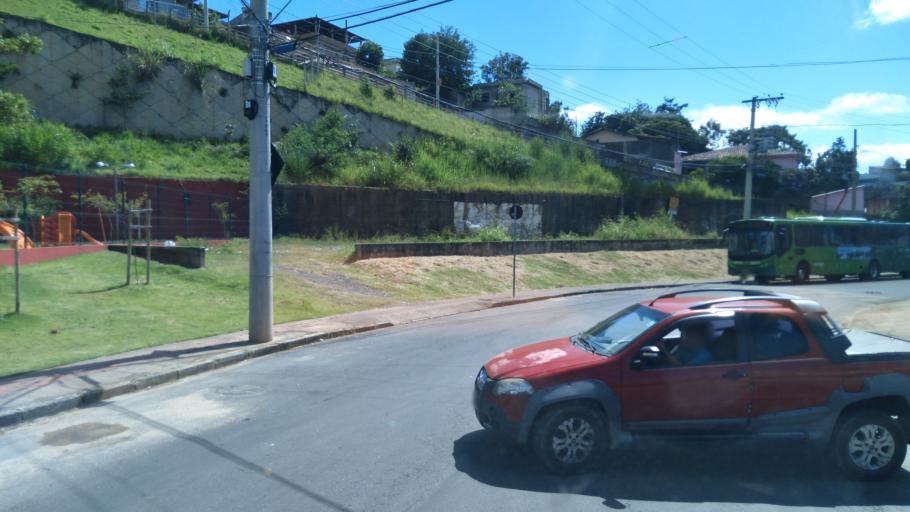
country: BR
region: Minas Gerais
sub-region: Belo Horizonte
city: Belo Horizonte
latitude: -19.8612
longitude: -43.9082
